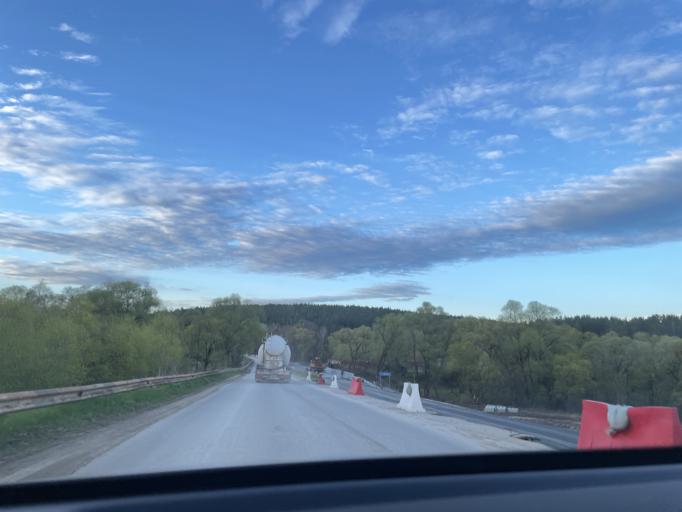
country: RU
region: Tula
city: Zaokskiy
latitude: 54.8167
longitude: 37.4334
